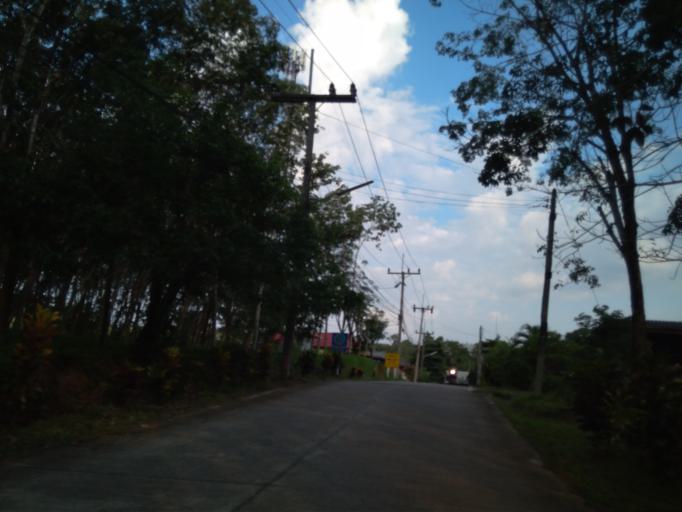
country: TH
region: Phangnga
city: Ko Yao
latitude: 8.1370
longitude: 98.6227
